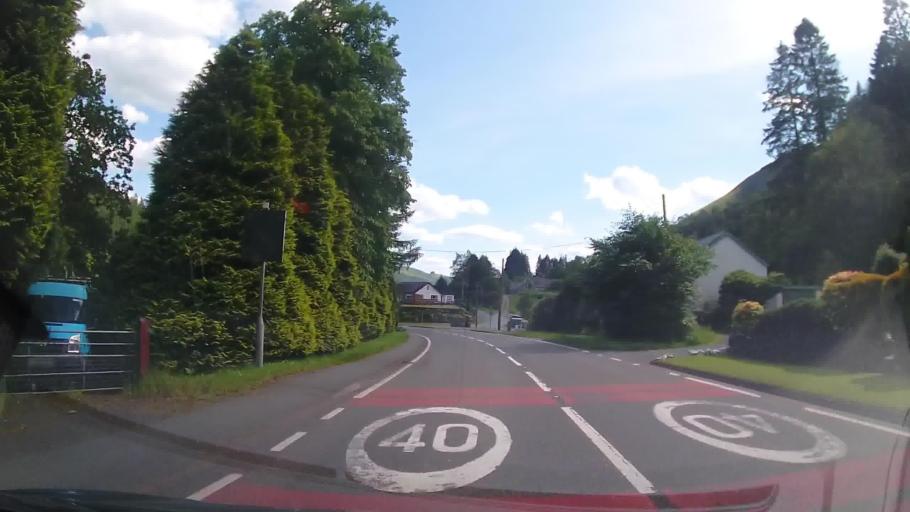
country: GB
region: Wales
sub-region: Gwynedd
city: Corris
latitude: 52.7137
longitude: -3.6911
